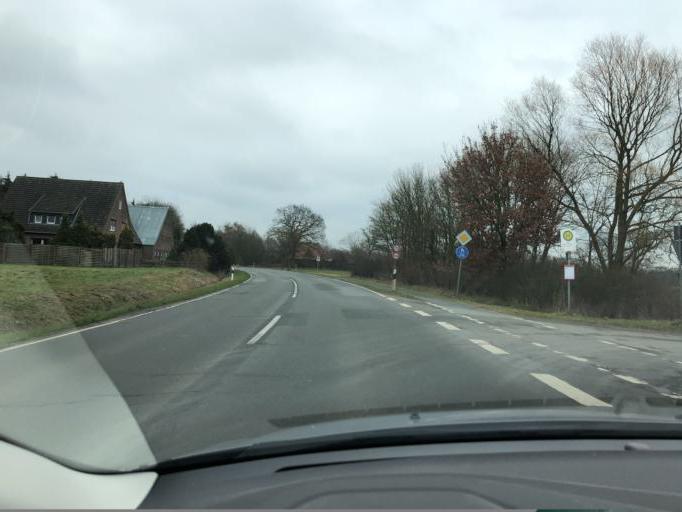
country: DE
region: Lower Saxony
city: Hude
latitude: 53.0920
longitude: 8.5052
